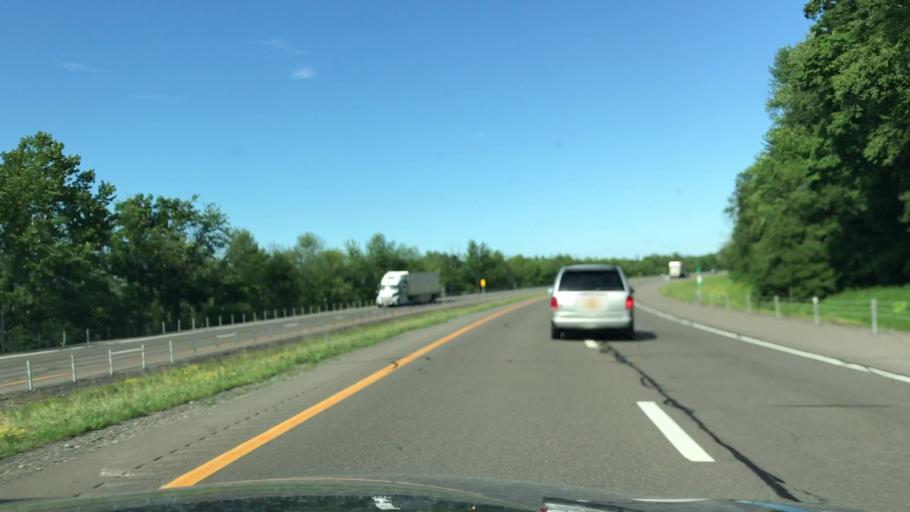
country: US
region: New York
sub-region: Tioga County
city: Owego
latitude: 42.0819
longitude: -76.3029
